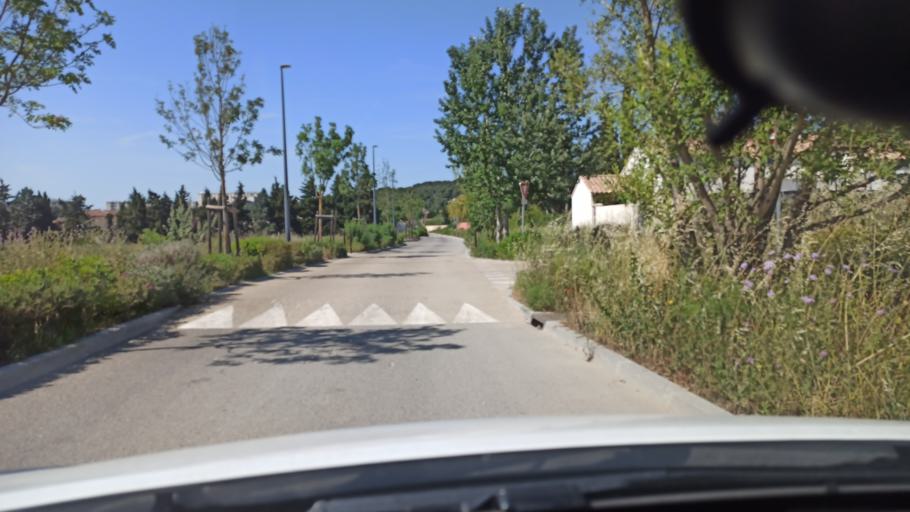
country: FR
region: Provence-Alpes-Cote d'Azur
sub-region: Departement des Bouches-du-Rhone
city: Chateaurenard
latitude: 43.8688
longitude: 4.8561
